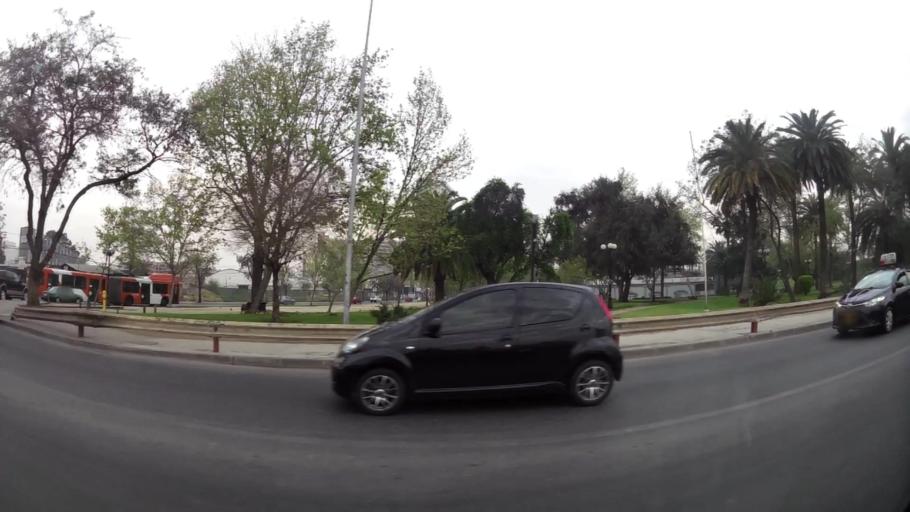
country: CL
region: Santiago Metropolitan
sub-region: Provincia de Santiago
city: Santiago
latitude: -33.4278
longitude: -70.6719
